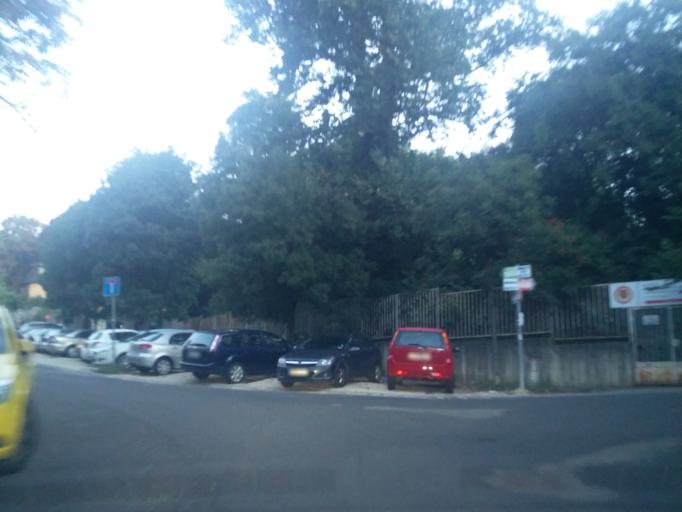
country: HU
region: Budapest
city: Budapest XI. keruelet
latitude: 47.4795
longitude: 19.0490
